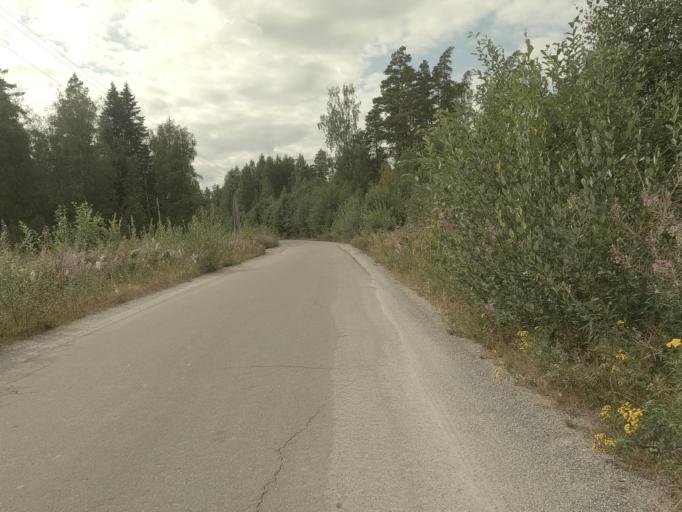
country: RU
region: Leningrad
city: Kamennogorsk
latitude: 60.9710
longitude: 29.1539
